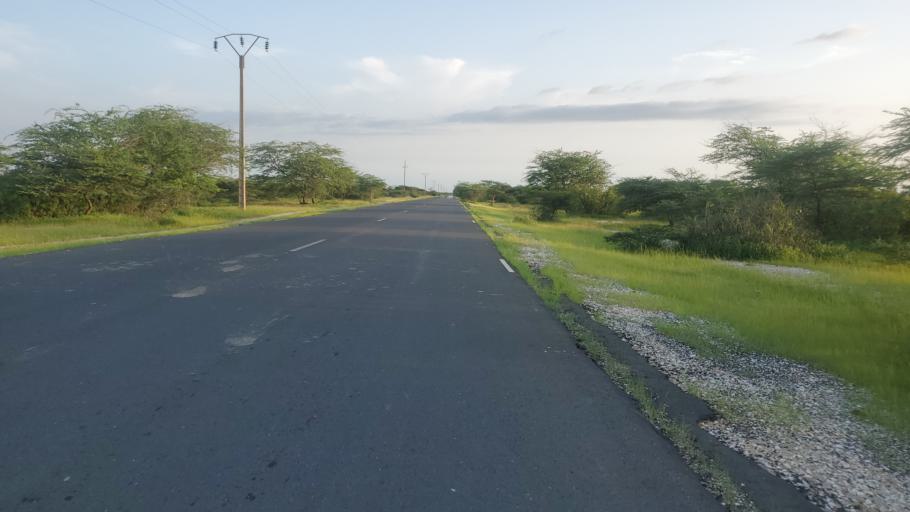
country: SN
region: Saint-Louis
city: Saint-Louis
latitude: 16.1858
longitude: -16.4094
